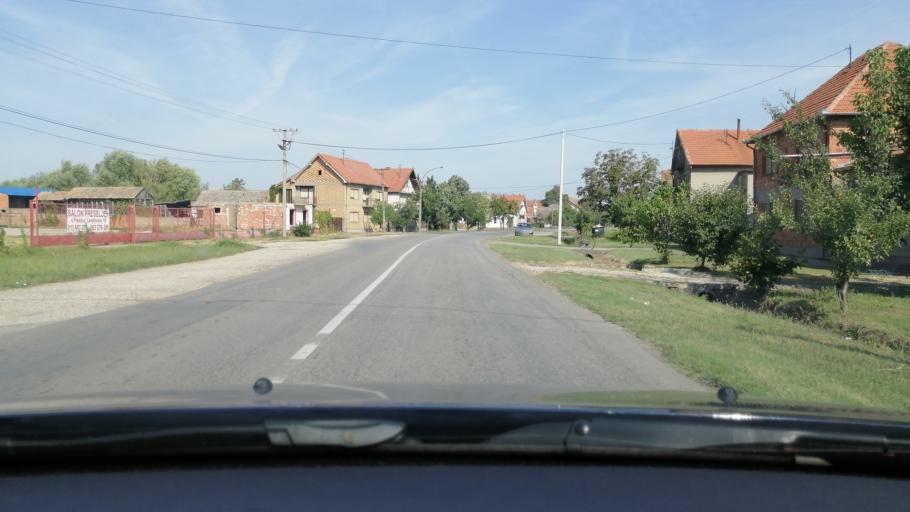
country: RS
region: Autonomna Pokrajina Vojvodina
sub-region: Juznobanatski Okrug
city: Kovacica
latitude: 45.1064
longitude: 20.6202
